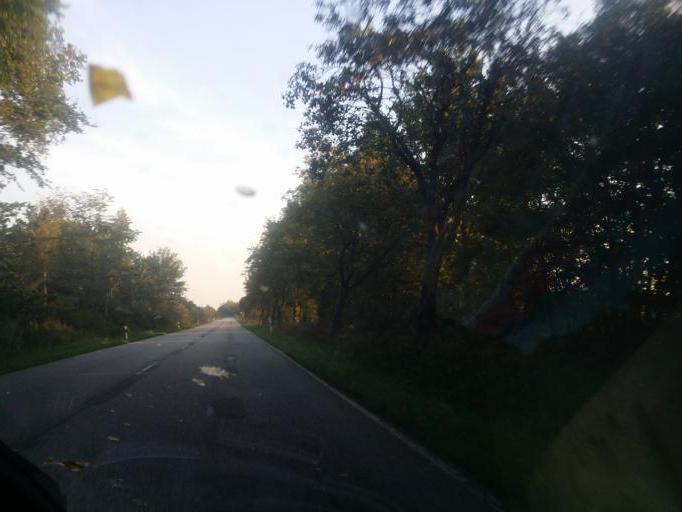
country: DE
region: Schleswig-Holstein
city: Hattstedt
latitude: 54.5176
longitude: 9.0328
